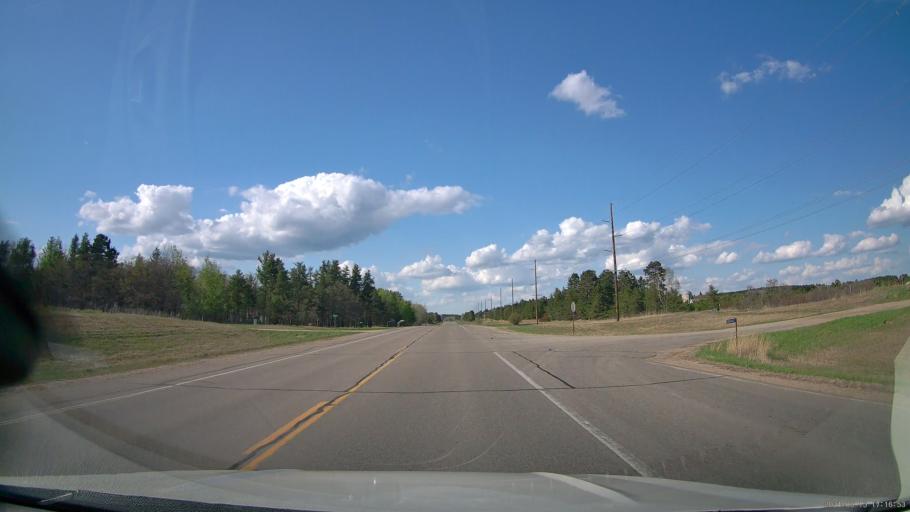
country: US
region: Minnesota
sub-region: Hubbard County
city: Park Rapids
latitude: 46.9357
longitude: -95.0168
